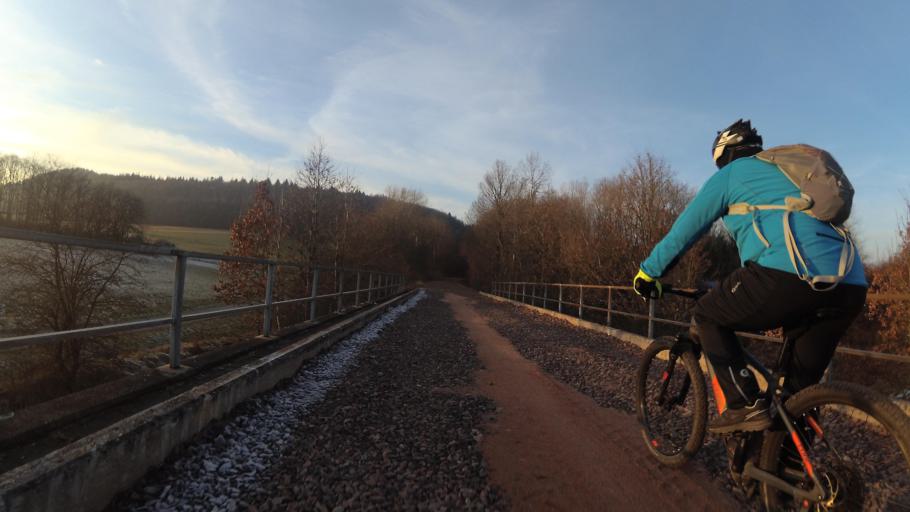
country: DE
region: Saarland
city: Nohfelden
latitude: 49.5695
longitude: 7.1645
